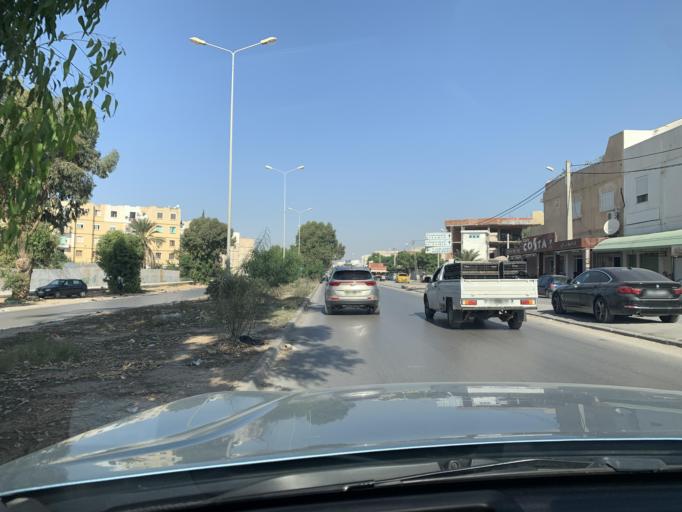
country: TN
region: Manouba
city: Manouba
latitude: 36.8213
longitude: 10.1237
